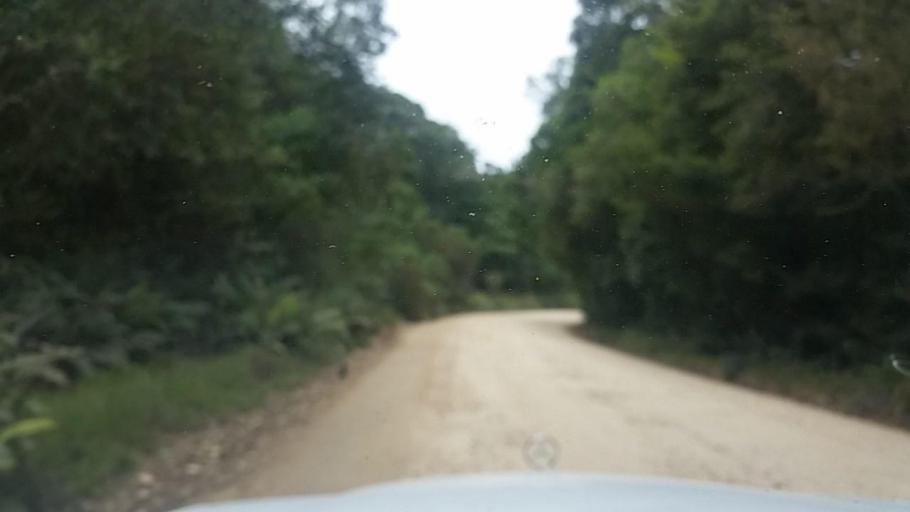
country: ZA
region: Western Cape
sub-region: Eden District Municipality
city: Knysna
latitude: -33.9580
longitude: 23.1560
